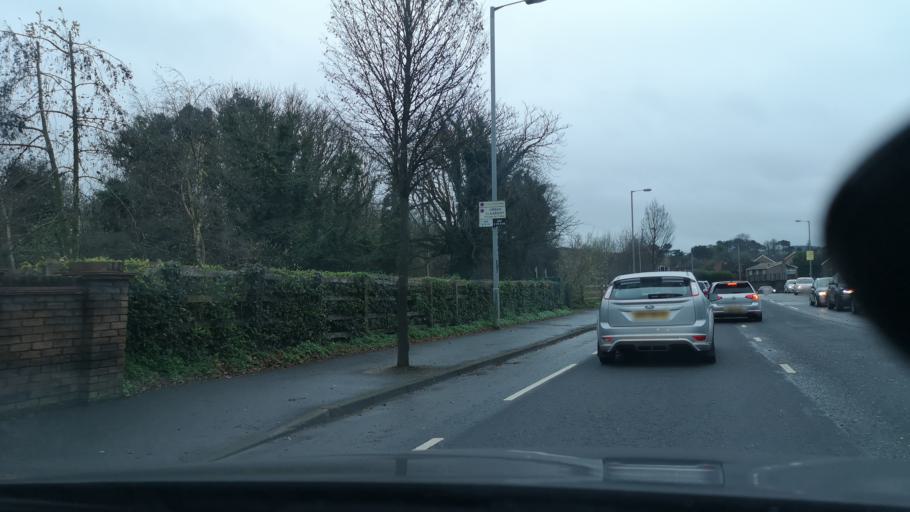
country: GB
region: Northern Ireland
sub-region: Castlereagh District
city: Castlereagh
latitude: 54.5911
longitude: -5.8555
